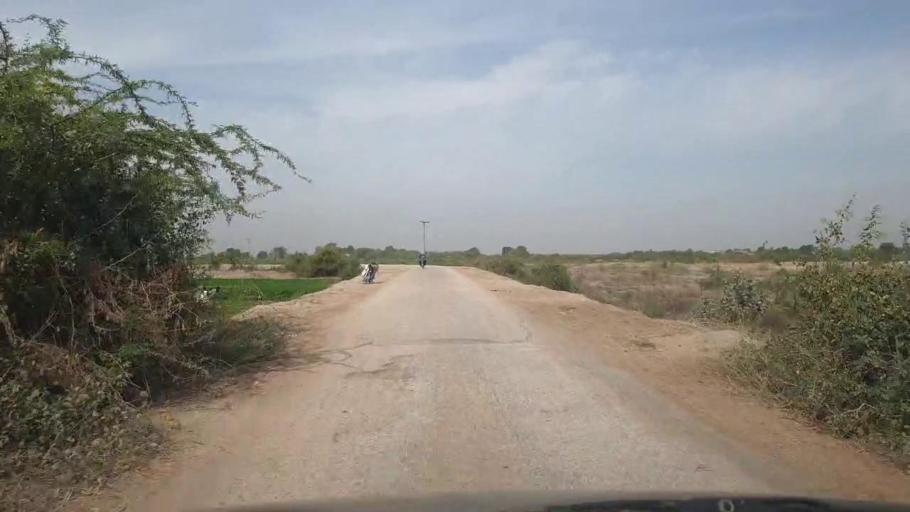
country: PK
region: Sindh
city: Kunri
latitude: 25.2281
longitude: 69.6752
